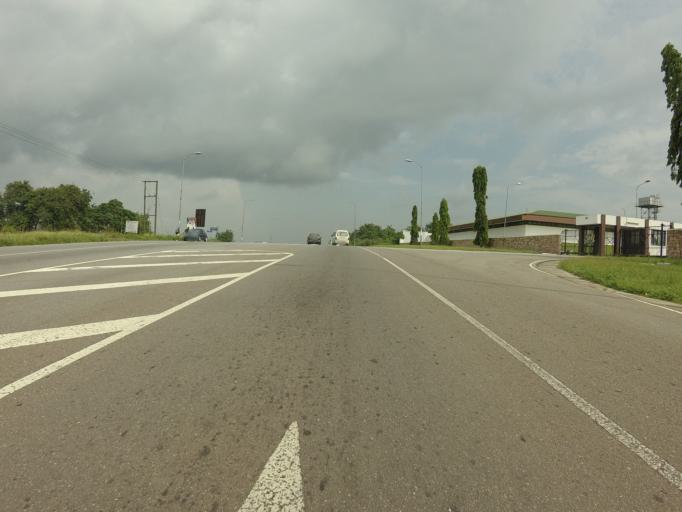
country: GH
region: Eastern
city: Aburi
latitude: 5.8071
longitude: -0.1817
